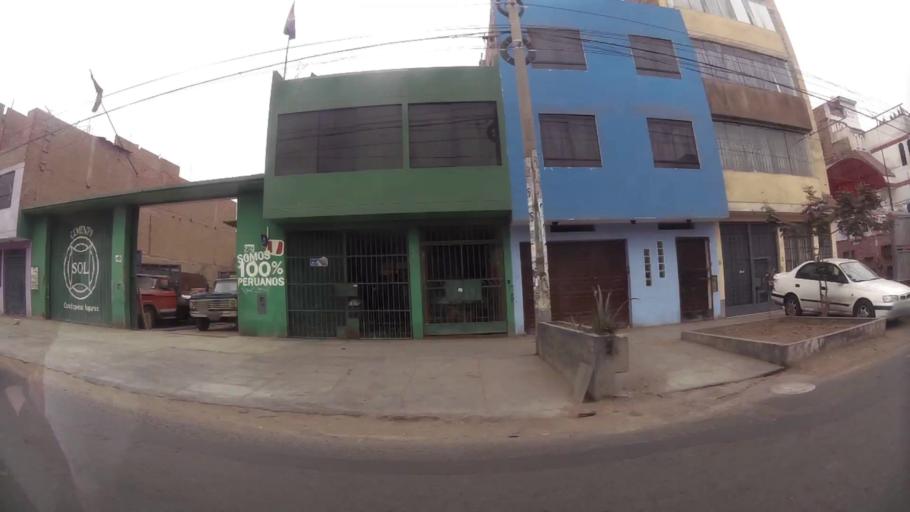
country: PE
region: Lima
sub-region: Lima
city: Independencia
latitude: -11.9508
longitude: -77.0767
